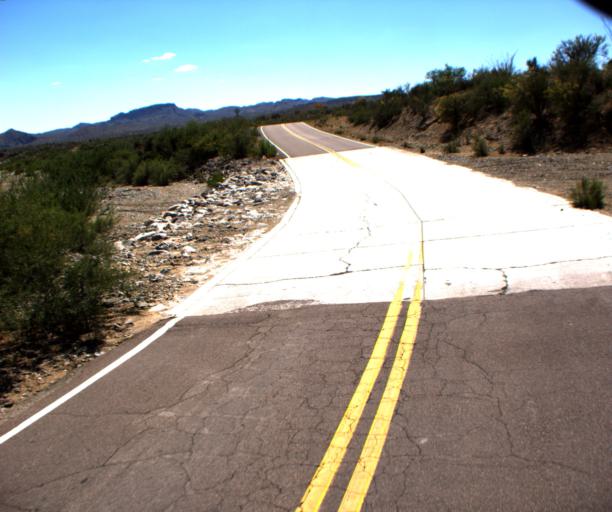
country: US
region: Arizona
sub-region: Yavapai County
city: Bagdad
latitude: 34.4661
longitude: -113.2268
